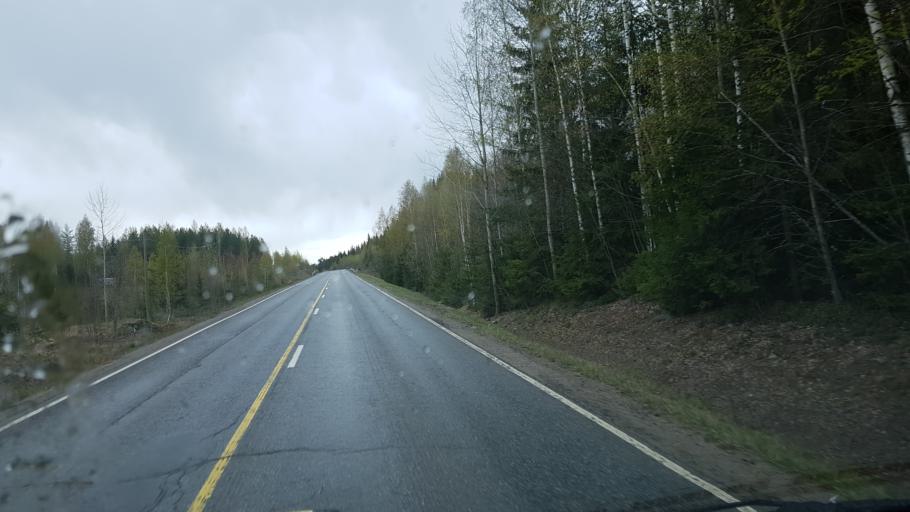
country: FI
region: Pirkanmaa
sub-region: Tampere
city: Pirkkala
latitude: 61.4022
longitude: 23.6308
